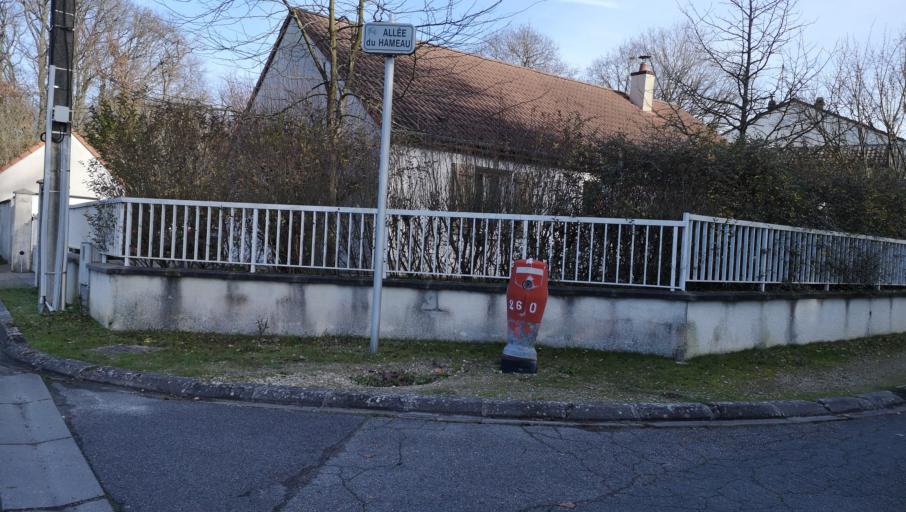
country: FR
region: Centre
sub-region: Departement du Loiret
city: Saran
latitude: 47.9554
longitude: 1.8999
